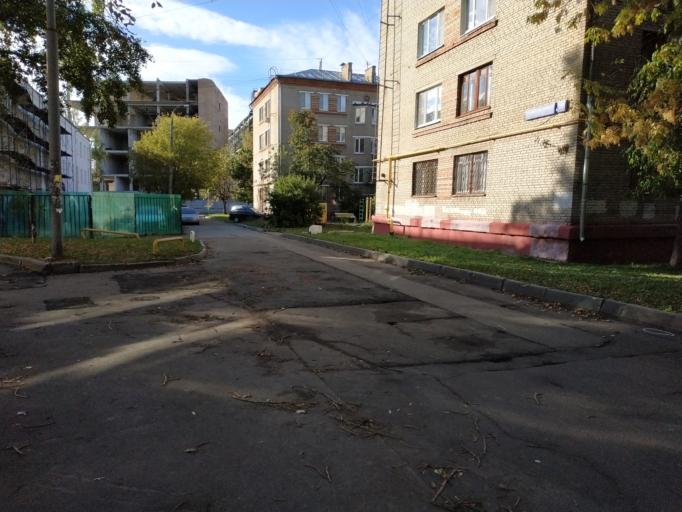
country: RU
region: Moskovskaya
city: Koptevo
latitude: 55.8120
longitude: 37.5278
